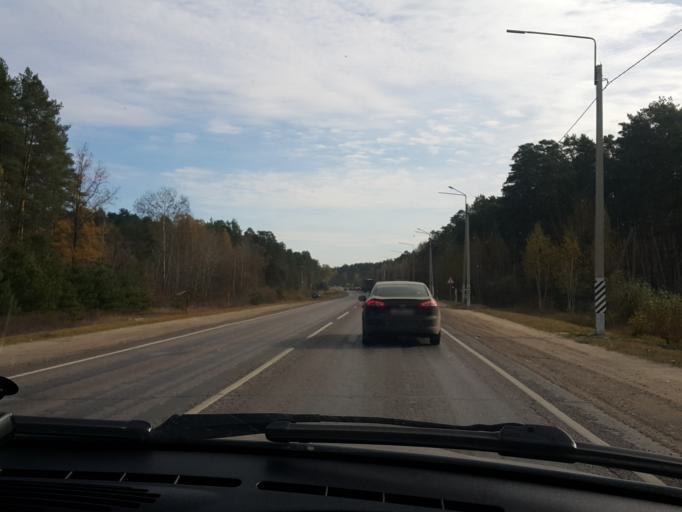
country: RU
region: Tambov
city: Donskoye
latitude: 52.7102
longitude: 41.5285
